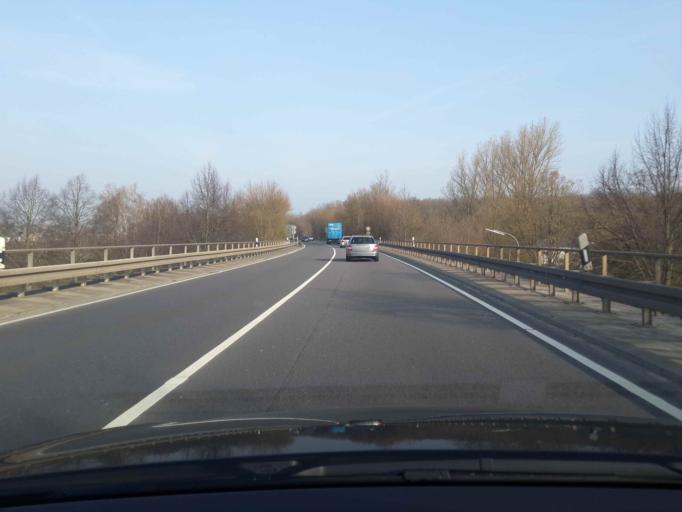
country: DE
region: Baden-Wuerttemberg
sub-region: Regierungsbezirk Stuttgart
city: Untereisesheim
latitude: 49.2287
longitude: 9.2062
